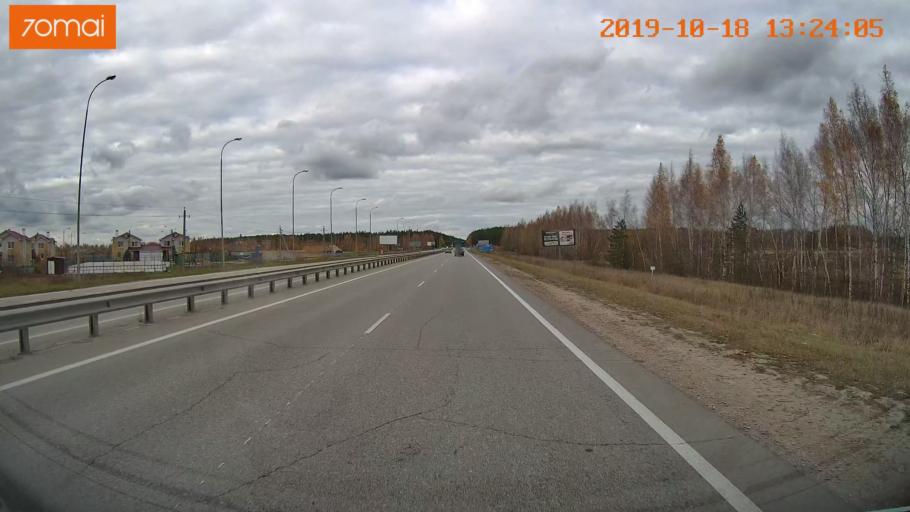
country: RU
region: Rjazan
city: Polyany
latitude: 54.7257
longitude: 39.8461
